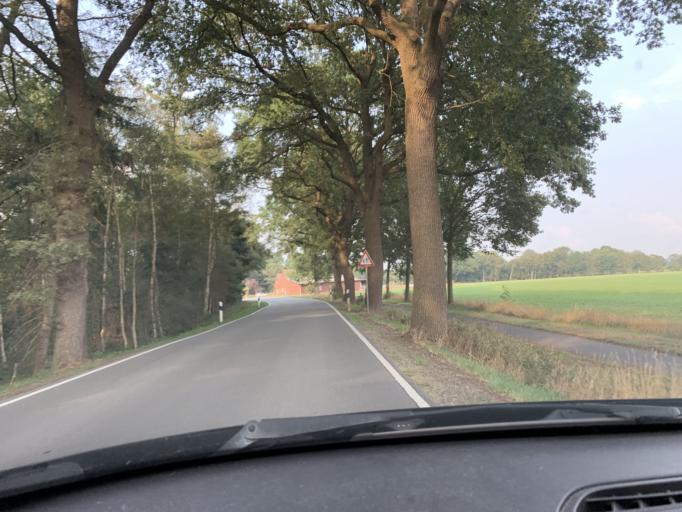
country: DE
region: Lower Saxony
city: Apen
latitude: 53.1977
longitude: 7.7915
